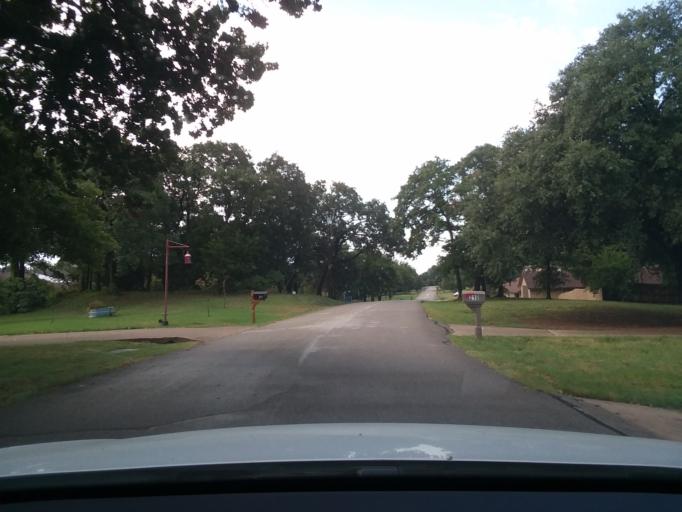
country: US
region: Texas
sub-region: Denton County
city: Double Oak
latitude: 33.0674
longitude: -97.1082
